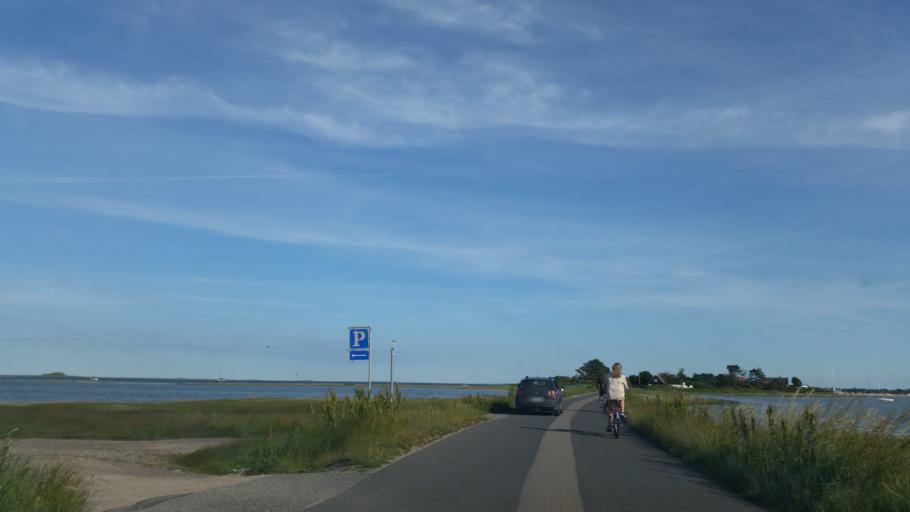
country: DK
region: Central Jutland
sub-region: Samso Kommune
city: Tranebjerg
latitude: 55.9158
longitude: 10.6380
